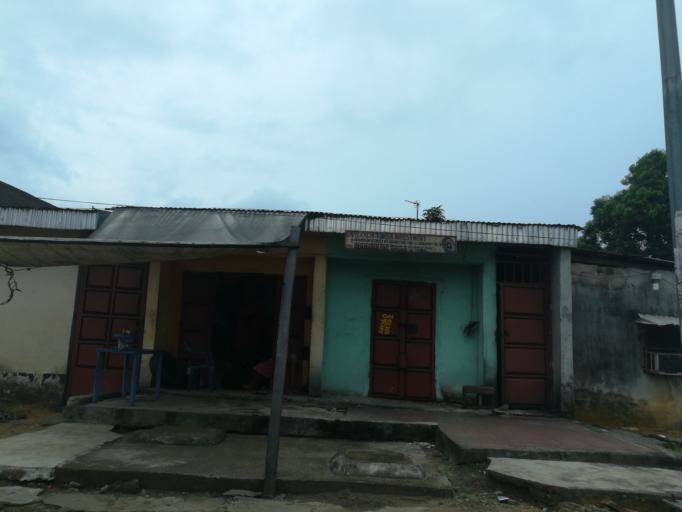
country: NG
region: Rivers
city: Port Harcourt
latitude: 4.7632
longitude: 7.0258
